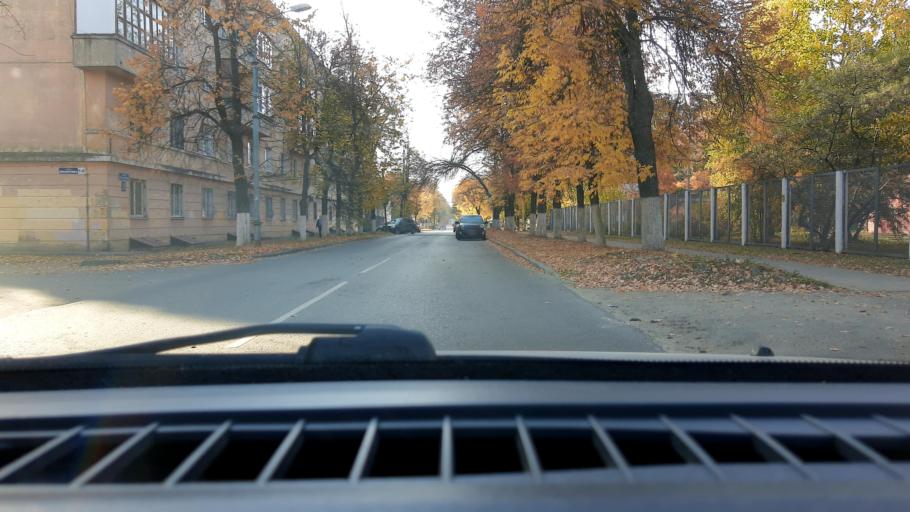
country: RU
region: Nizjnij Novgorod
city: Gorbatovka
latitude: 56.2503
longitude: 43.8619
